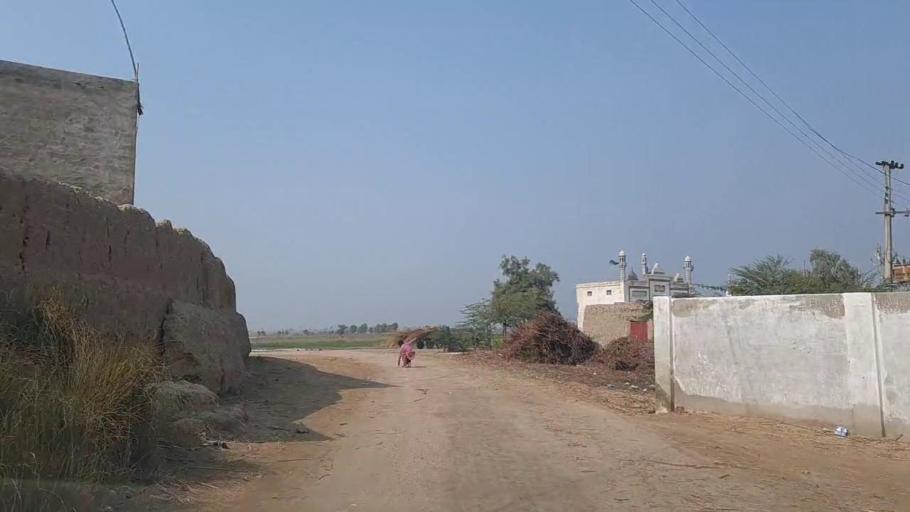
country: PK
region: Sindh
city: Daur
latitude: 26.4328
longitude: 68.4426
